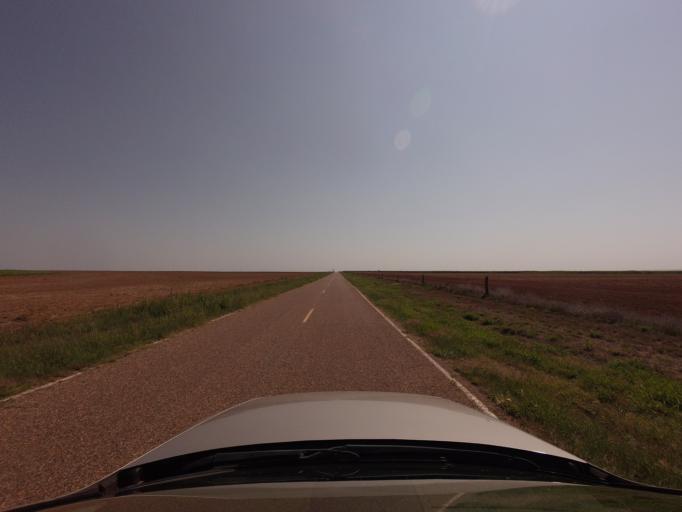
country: US
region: New Mexico
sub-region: Curry County
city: Cannon Air Force Base
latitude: 34.6330
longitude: -103.3579
